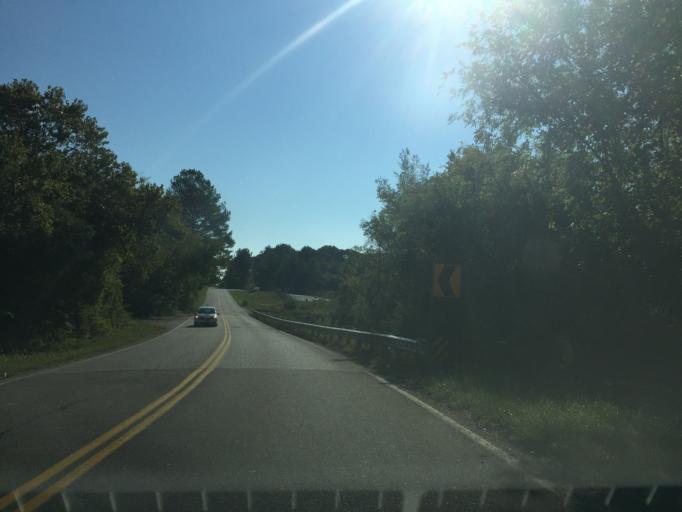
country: US
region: Tennessee
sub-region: Hamilton County
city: Harrison
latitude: 35.0837
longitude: -85.1596
